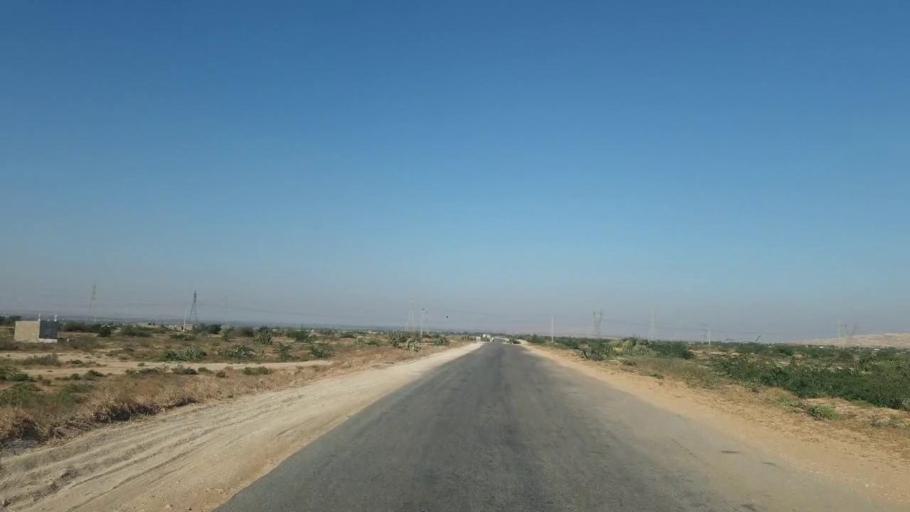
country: PK
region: Sindh
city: Gharo
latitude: 25.1694
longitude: 67.6601
